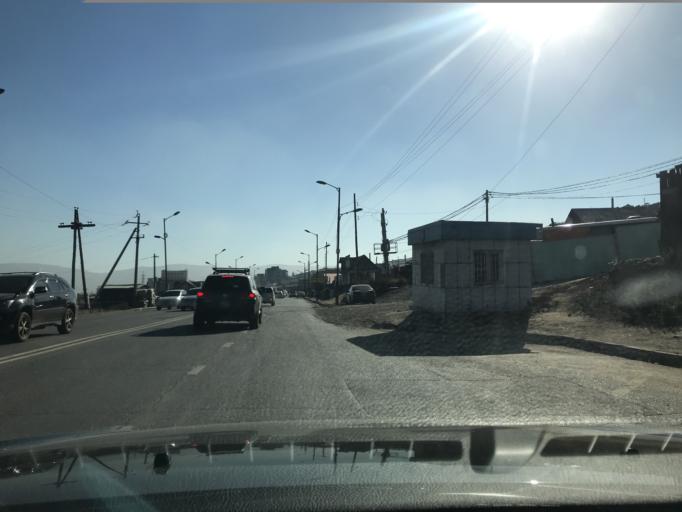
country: MN
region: Ulaanbaatar
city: Ulaanbaatar
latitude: 47.9741
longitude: 106.9180
